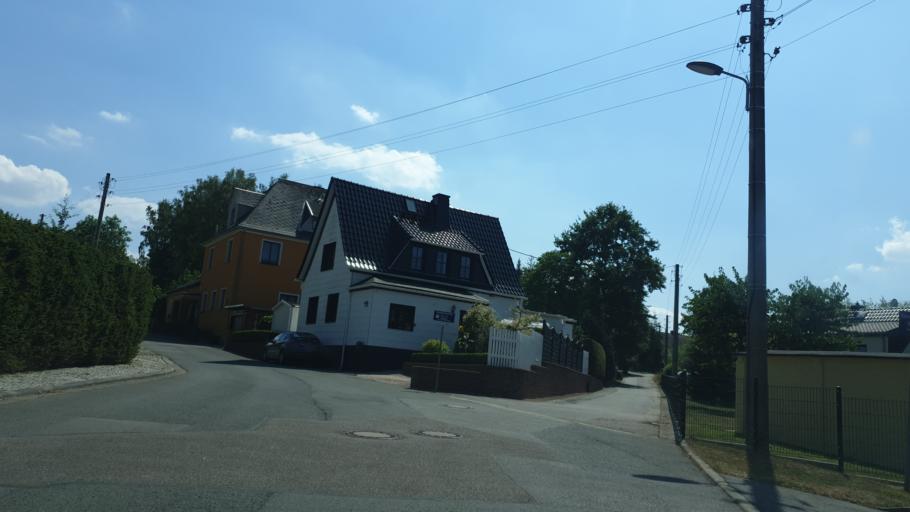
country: DE
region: Saxony
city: Gersdorf
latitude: 50.7463
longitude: 12.7109
